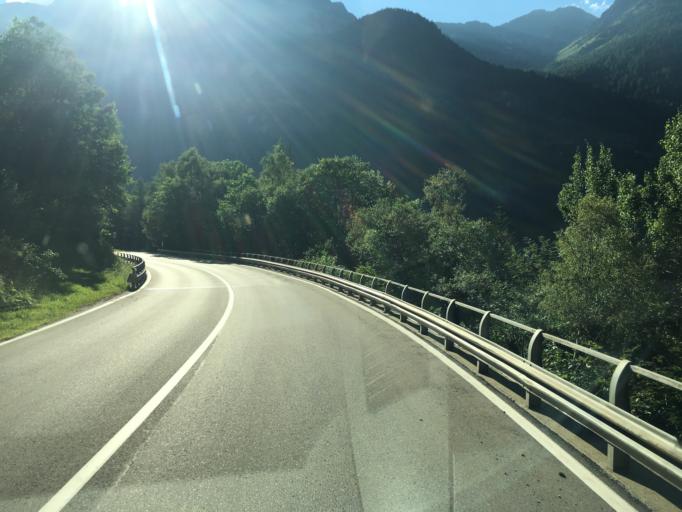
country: CH
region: Valais
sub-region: Saint-Maurice District
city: Salvan
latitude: 46.0713
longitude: 6.9769
